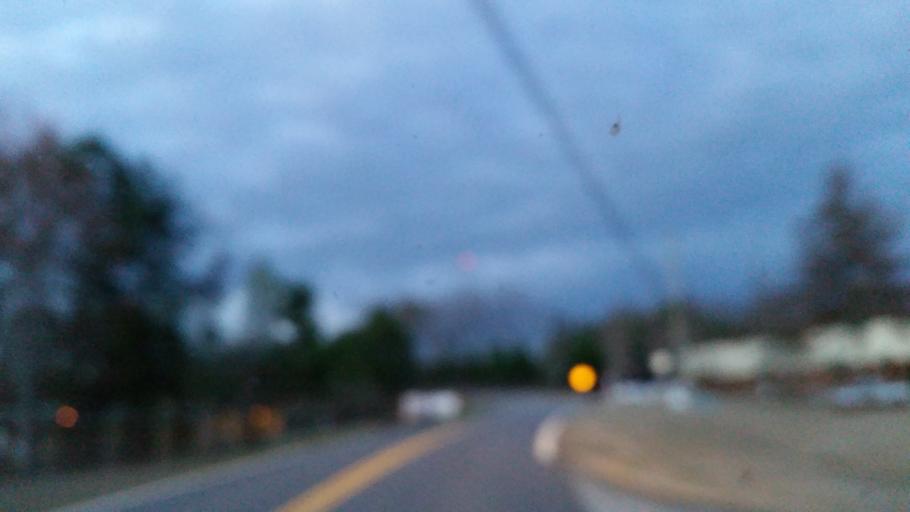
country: US
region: Georgia
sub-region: Cherokee County
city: Ball Ground
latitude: 34.3046
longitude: -84.4267
